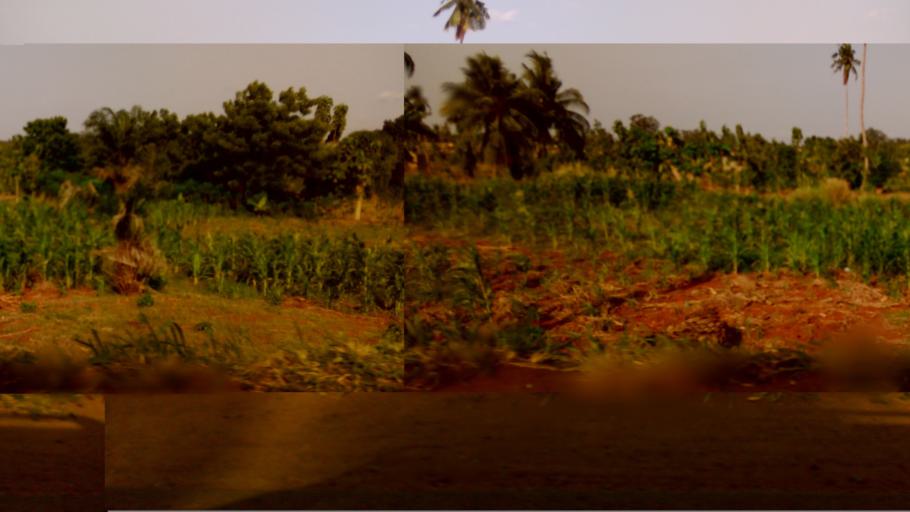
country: TG
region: Maritime
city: Tsevie
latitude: 6.3823
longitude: 1.2034
